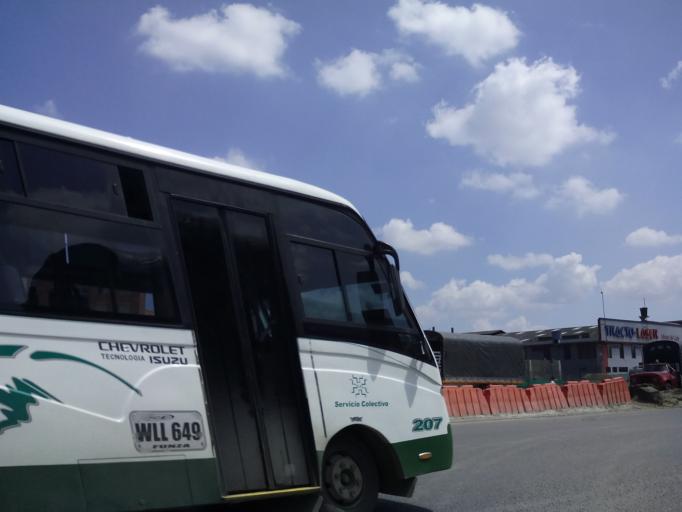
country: CO
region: Bogota D.C.
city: Bogota
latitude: 4.6647
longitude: -74.1430
